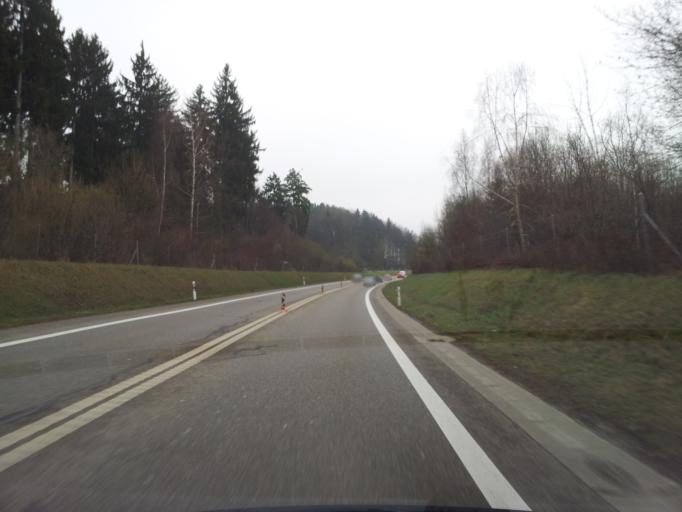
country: CH
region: Zurich
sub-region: Bezirk Andelfingen
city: Henggart
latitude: 47.5490
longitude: 8.6875
